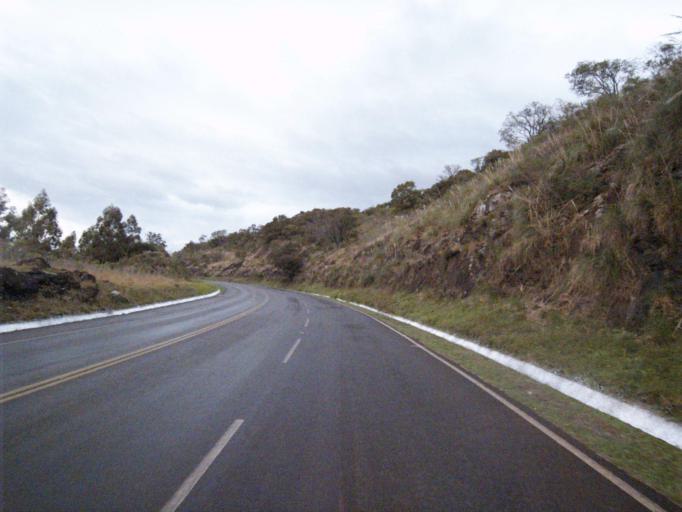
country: BR
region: Santa Catarina
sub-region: Concordia
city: Concordia
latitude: -27.0566
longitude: -51.8902
